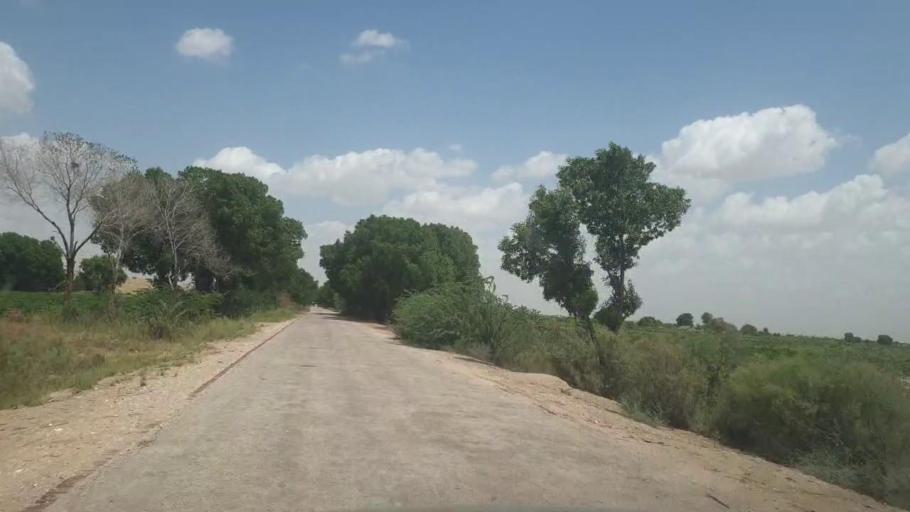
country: PK
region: Sindh
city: Kot Diji
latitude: 27.2202
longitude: 69.0442
